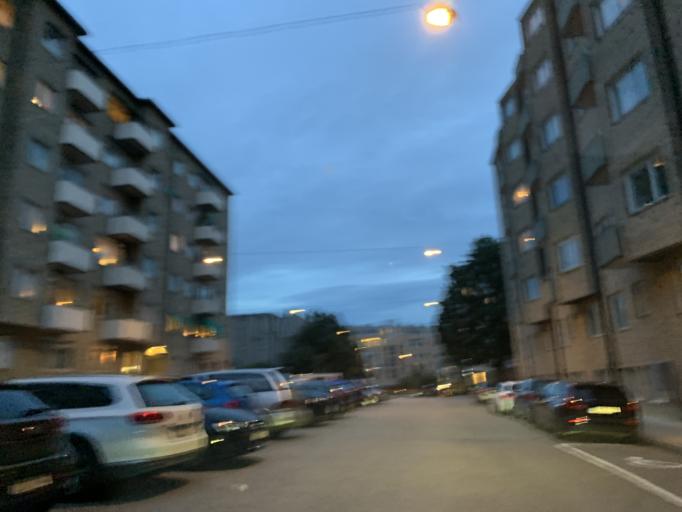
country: SE
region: Stockholm
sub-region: Solna Kommun
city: Solna
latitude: 59.3277
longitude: 18.0131
